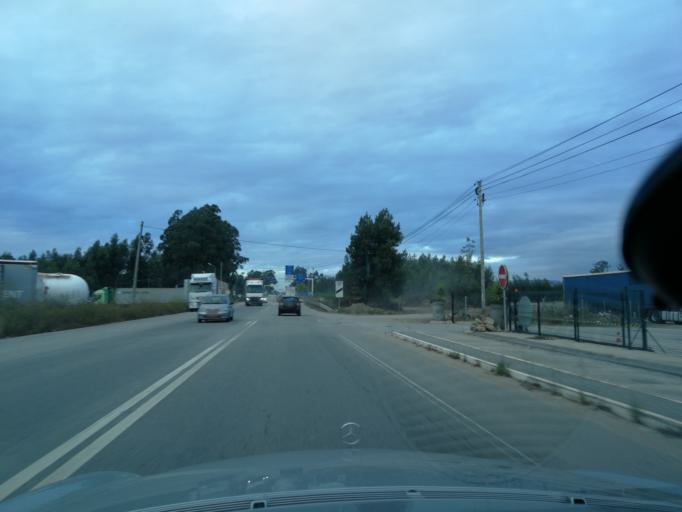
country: PT
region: Aveiro
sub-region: Albergaria-A-Velha
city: Albergaria-a-Velha
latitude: 40.6708
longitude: -8.4739
